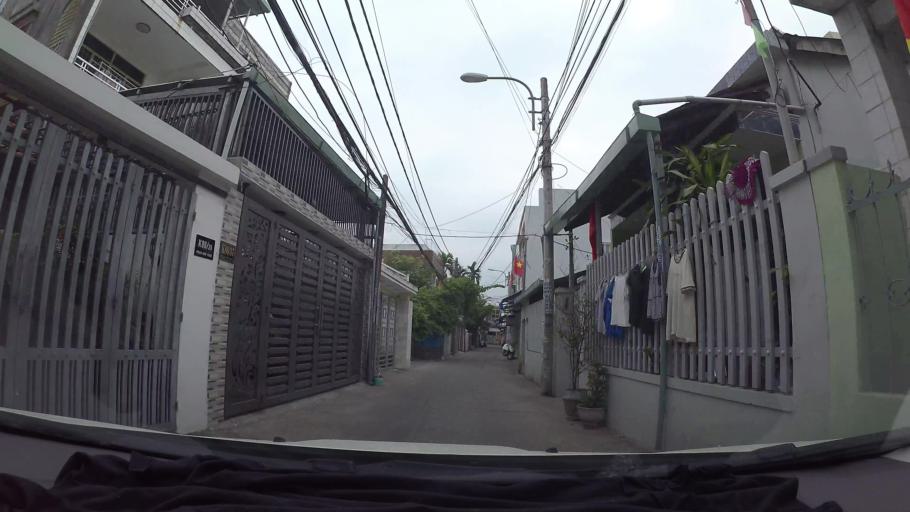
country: VN
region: Da Nang
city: Thanh Khe
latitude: 16.0621
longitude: 108.1886
